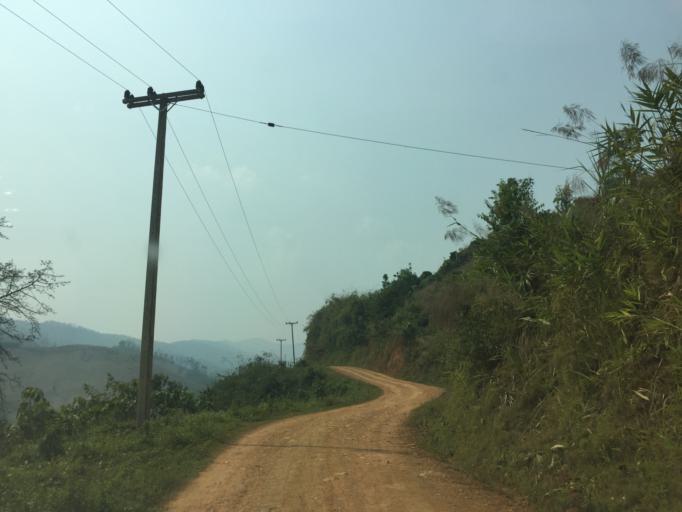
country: TH
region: Phayao
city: Phu Sang
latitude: 19.5795
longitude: 100.5276
